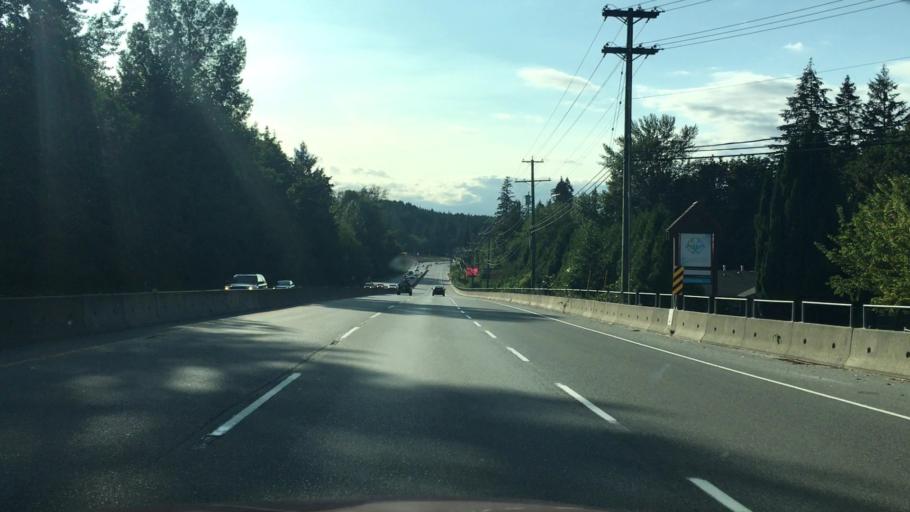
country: CA
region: British Columbia
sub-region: Cowichan Valley Regional District
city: Ladysmith
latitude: 49.0122
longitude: -123.8440
